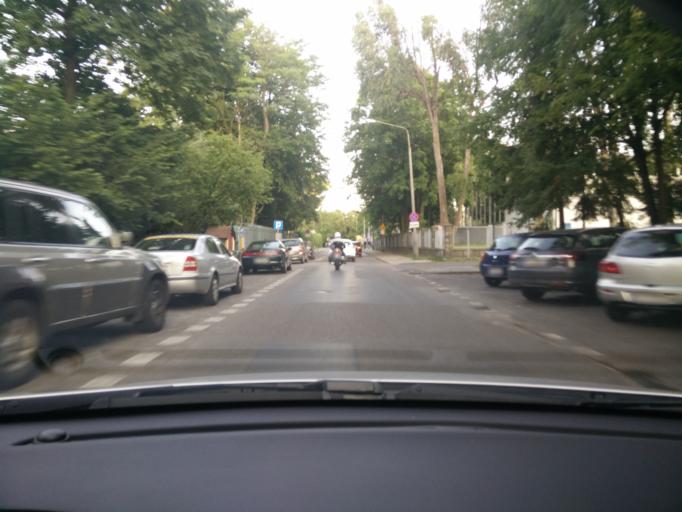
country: PL
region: Pomeranian Voivodeship
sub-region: Sopot
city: Sopot
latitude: 54.4504
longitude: 18.5621
